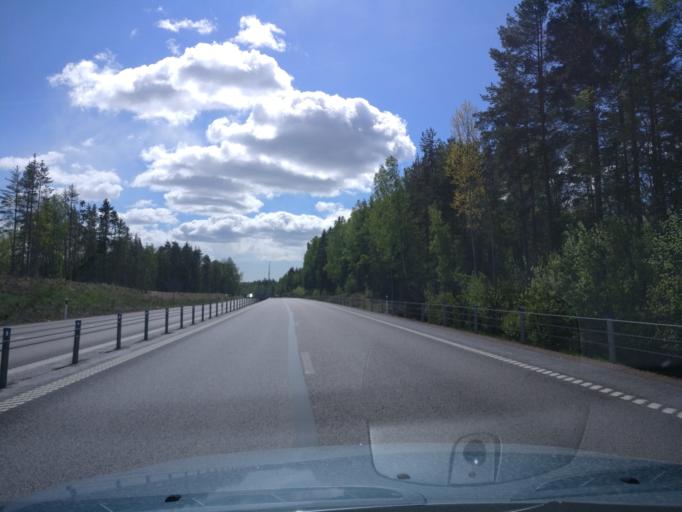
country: SE
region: Vaermland
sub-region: Karlstads Kommun
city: Karlstad
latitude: 59.4056
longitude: 13.5317
